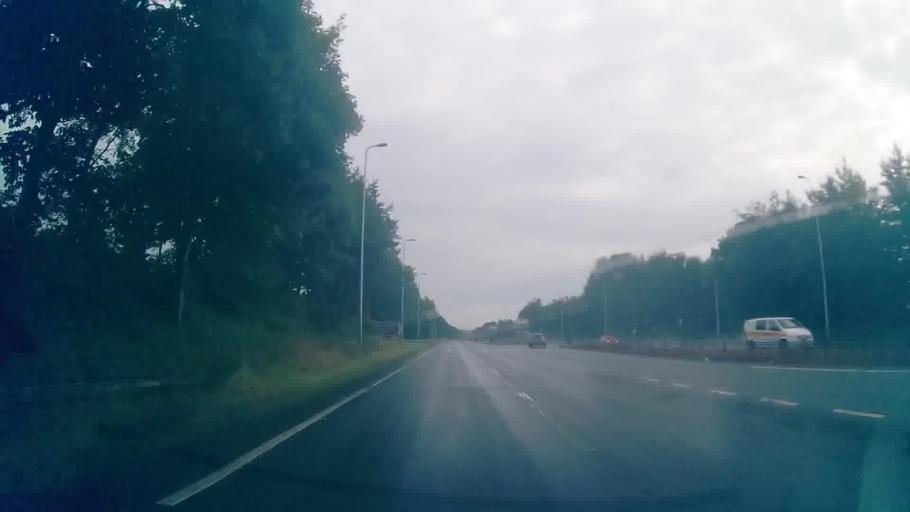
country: GB
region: Scotland
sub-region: Dumfries and Galloway
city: Locharbriggs
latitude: 55.0667
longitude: -3.5214
